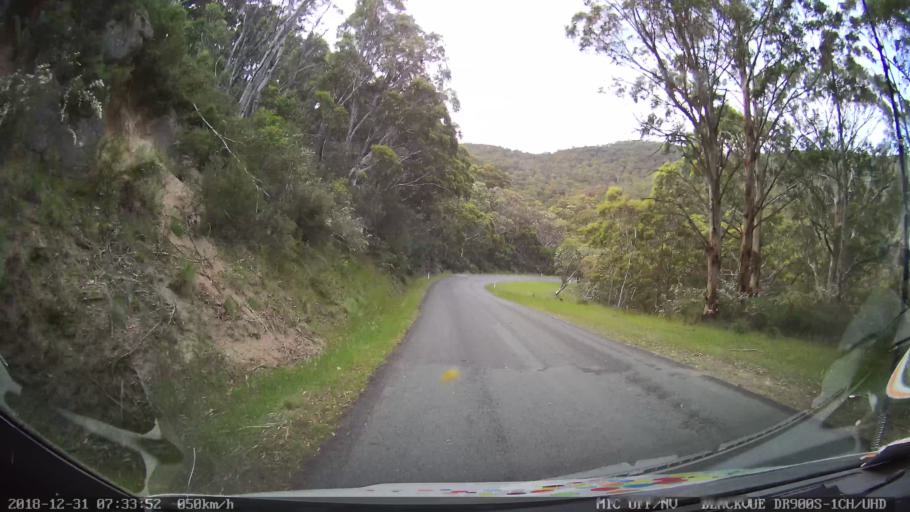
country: AU
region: New South Wales
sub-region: Snowy River
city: Jindabyne
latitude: -36.3342
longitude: 148.4545
